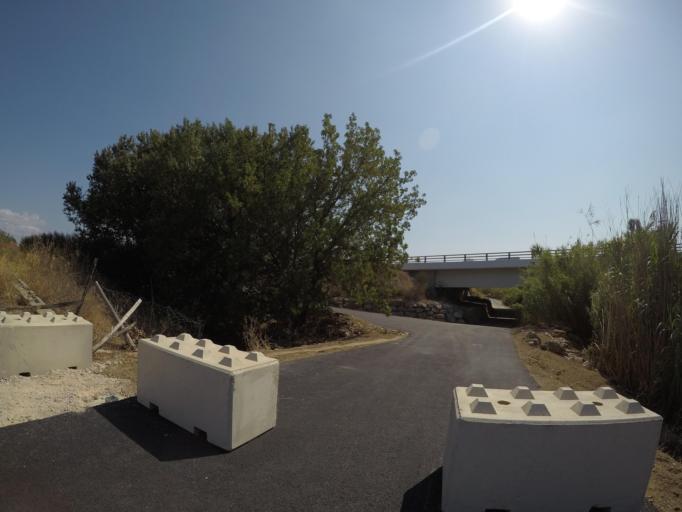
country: FR
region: Languedoc-Roussillon
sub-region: Departement des Pyrenees-Orientales
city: Saint-Esteve
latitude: 42.6996
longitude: 2.8629
